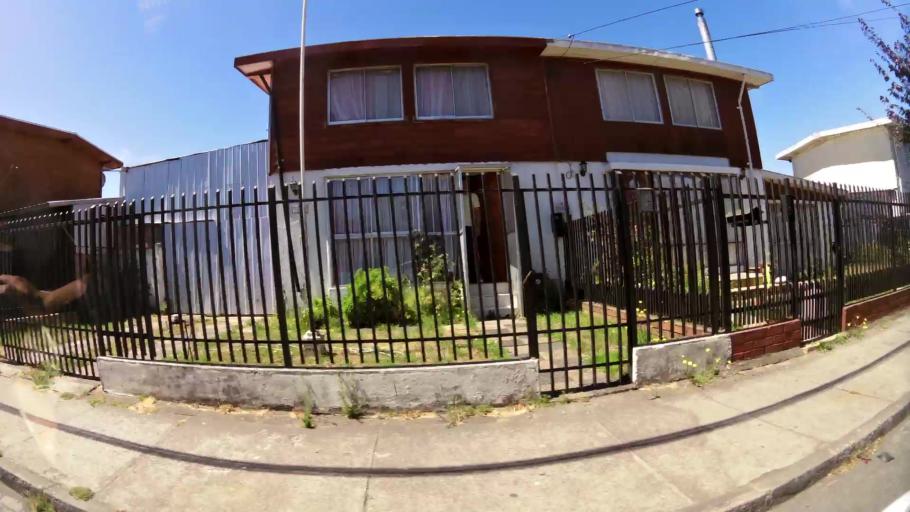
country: CL
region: Biobio
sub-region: Provincia de Concepcion
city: Talcahuano
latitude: -36.7584
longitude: -73.0939
